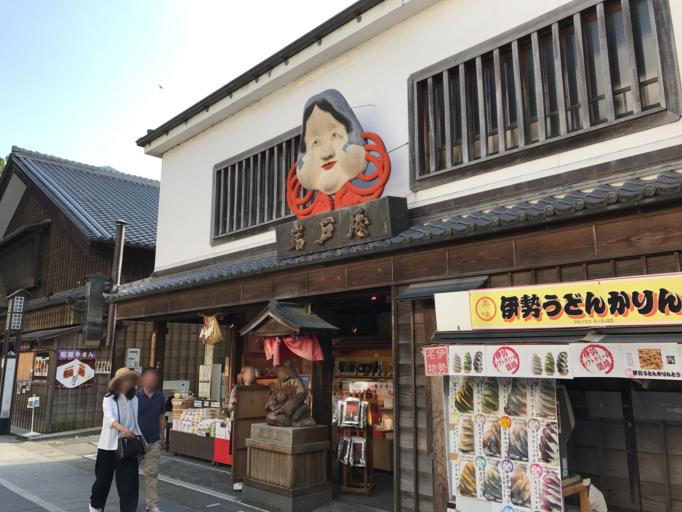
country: JP
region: Mie
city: Ise
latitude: 34.4600
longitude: 136.7232
